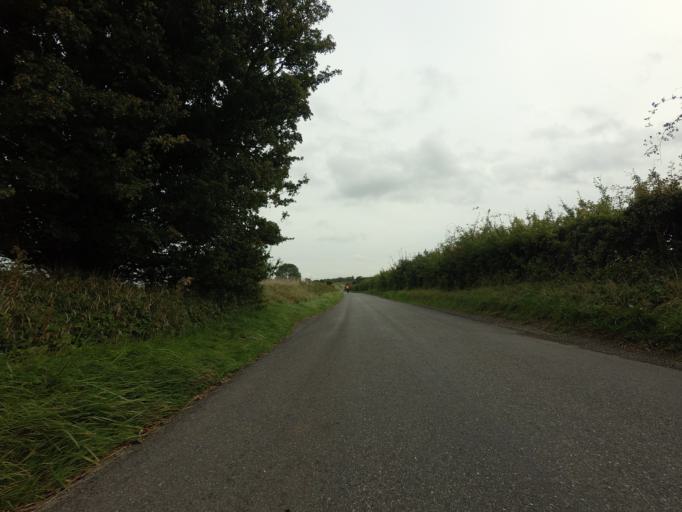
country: GB
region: England
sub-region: Hertfordshire
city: Buntingford
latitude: 51.9770
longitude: 0.0598
